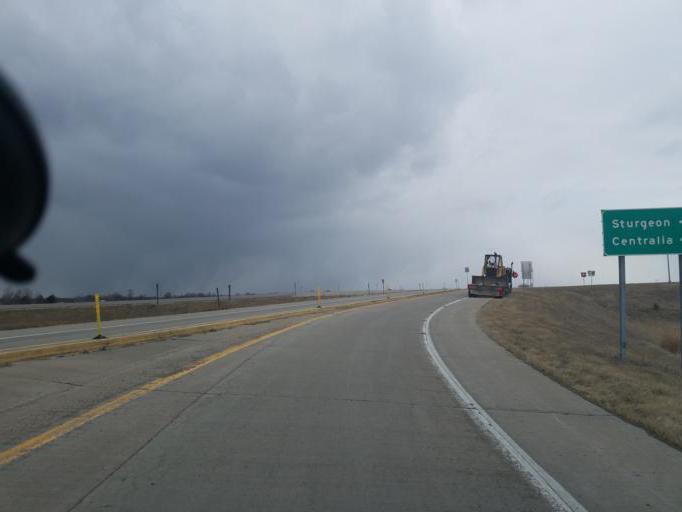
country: US
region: Missouri
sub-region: Boone County
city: Hallsville
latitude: 39.2444
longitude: -92.3258
